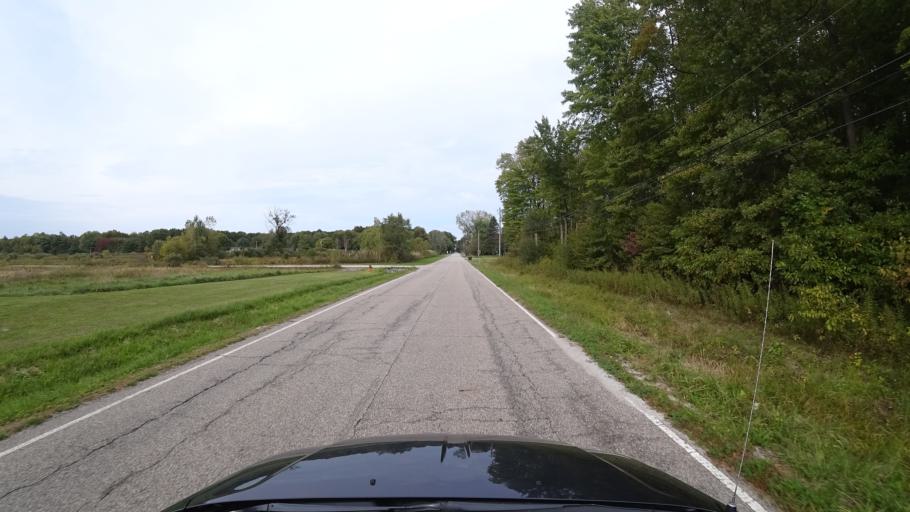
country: US
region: Indiana
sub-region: LaPorte County
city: Long Beach
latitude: 41.7212
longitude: -86.8162
